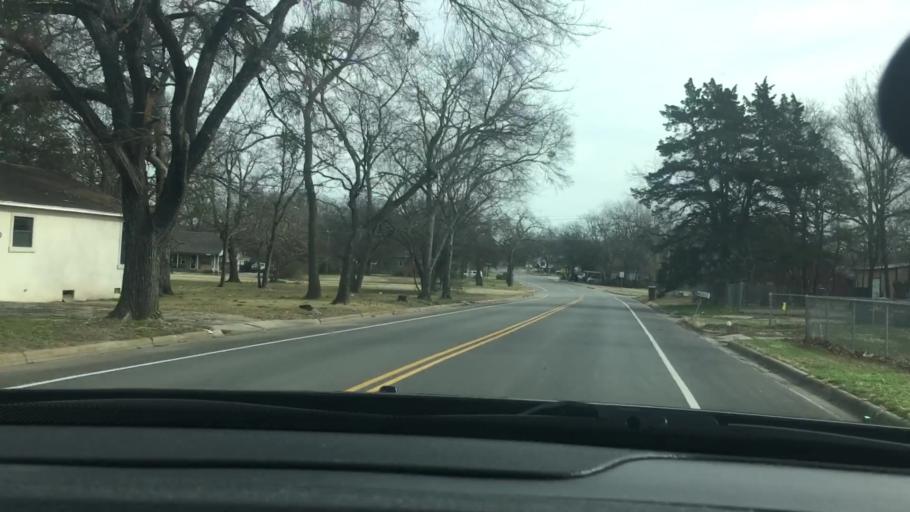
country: US
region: Oklahoma
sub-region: Carter County
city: Ardmore
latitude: 34.1763
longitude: -97.1174
